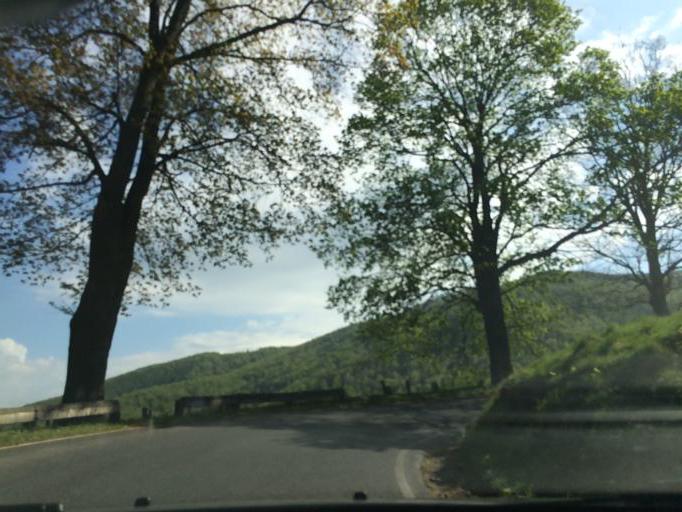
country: PL
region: Lower Silesian Voivodeship
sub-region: Powiat klodzki
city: Jugow
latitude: 50.6673
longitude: 16.5390
